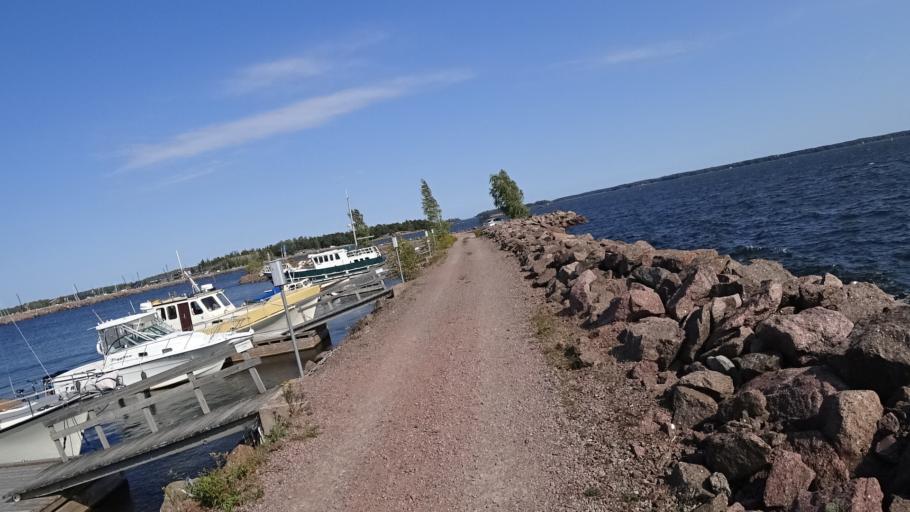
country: FI
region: Kymenlaakso
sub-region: Kotka-Hamina
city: Kotka
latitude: 60.4564
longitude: 26.9553
